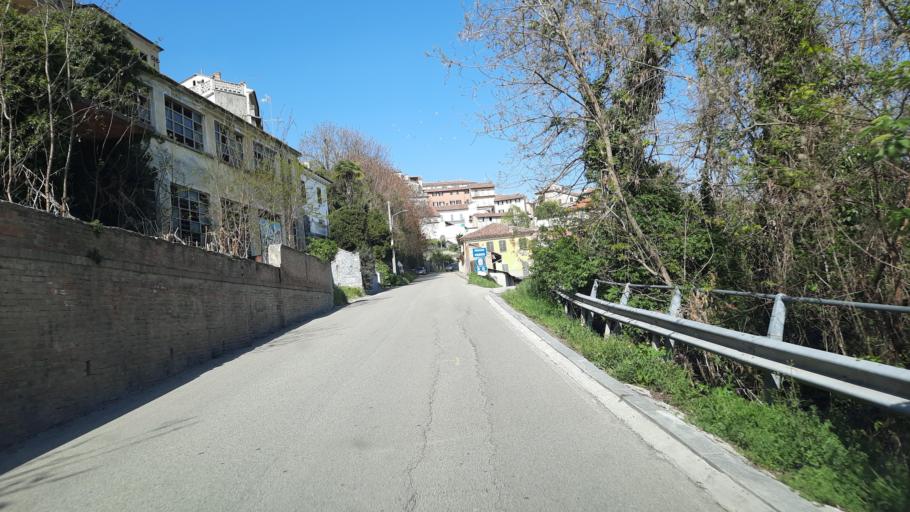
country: IT
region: Piedmont
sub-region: Provincia di Alessandria
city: Vignale Monferrato
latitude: 45.0085
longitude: 8.3966
